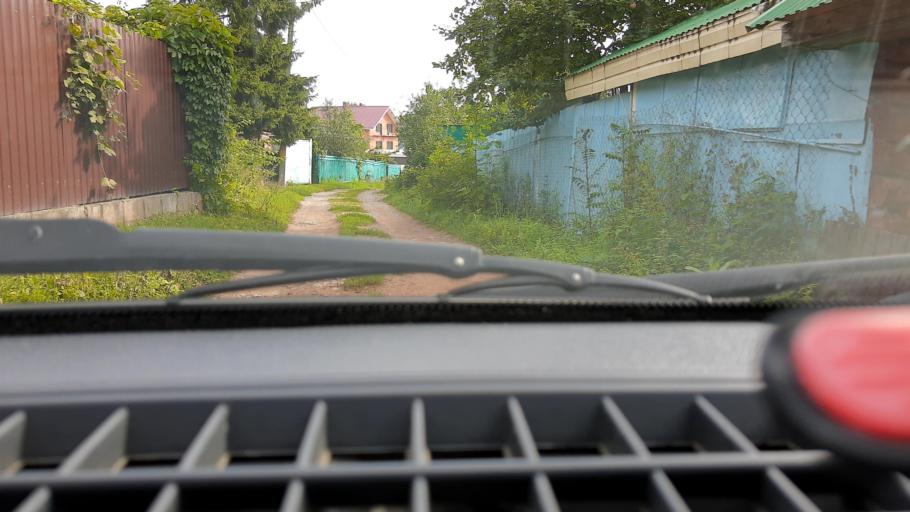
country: RU
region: Bashkortostan
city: Avdon
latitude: 54.6133
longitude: 55.6274
